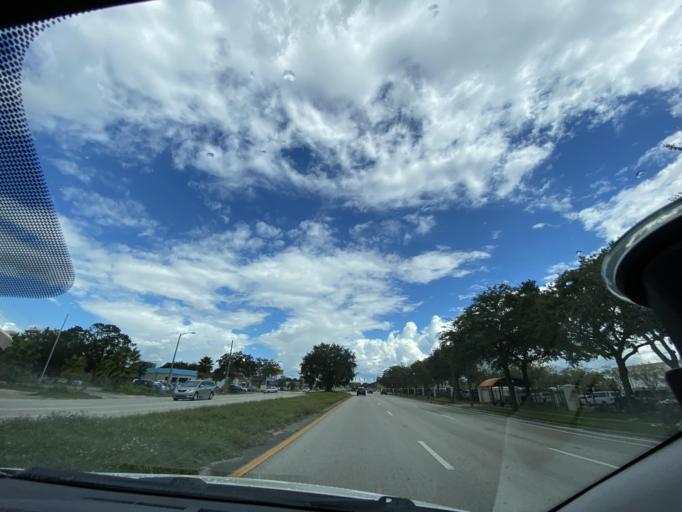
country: US
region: Florida
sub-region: Orange County
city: Orlando
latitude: 28.5527
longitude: -81.4125
